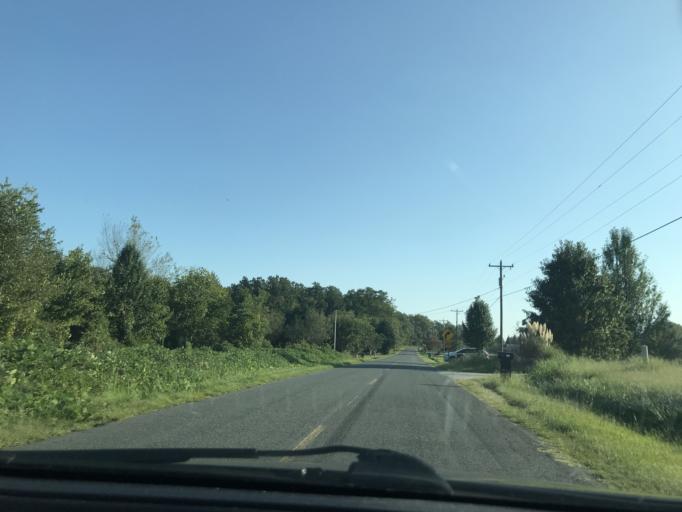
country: US
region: South Carolina
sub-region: Cherokee County
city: Gaffney
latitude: 35.1524
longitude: -81.7417
